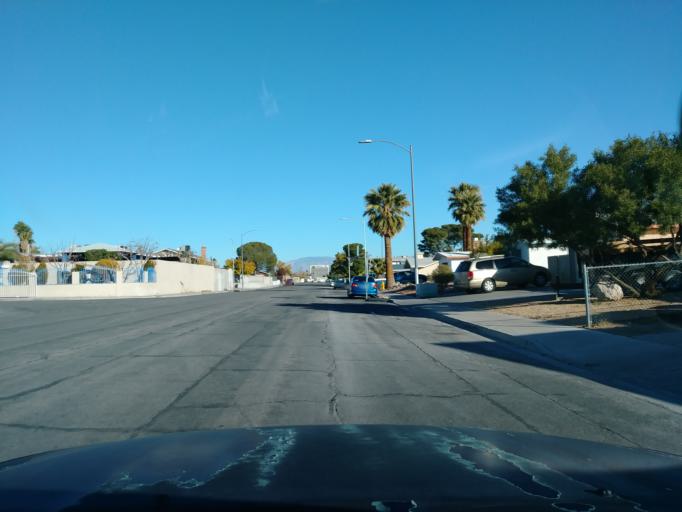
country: US
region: Nevada
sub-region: Clark County
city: Spring Valley
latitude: 36.1627
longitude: -115.2468
